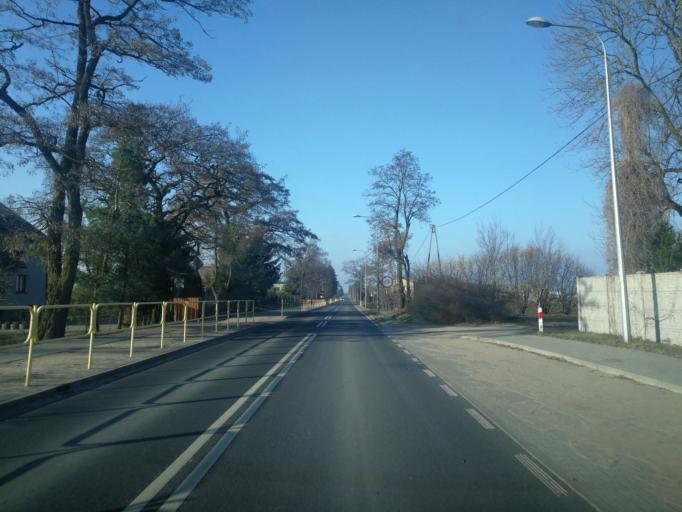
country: PL
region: Warmian-Masurian Voivodeship
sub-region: Powiat ilawski
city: Lubawa
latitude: 53.4744
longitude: 19.7671
